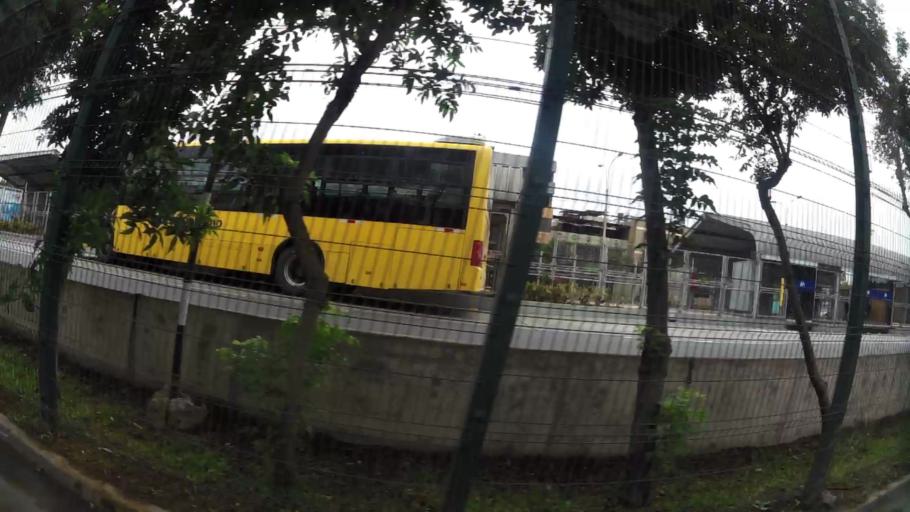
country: PE
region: Lima
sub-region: Lima
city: Surco
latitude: -12.1809
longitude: -77.0083
